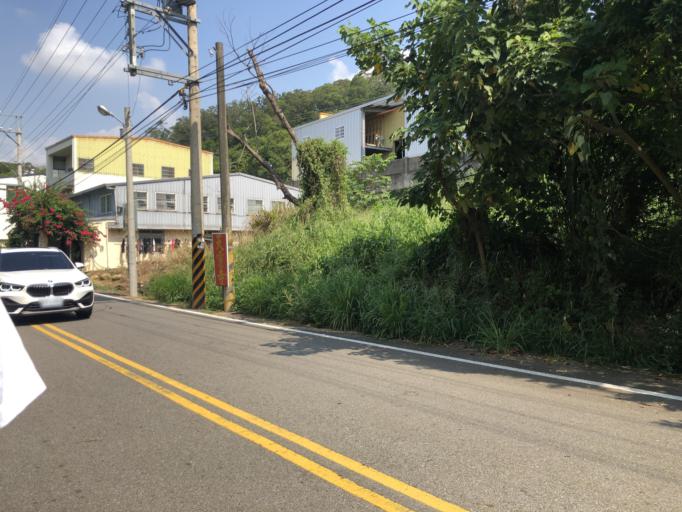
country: TW
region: Taiwan
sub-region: Miaoli
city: Miaoli
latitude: 24.4737
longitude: 120.7953
